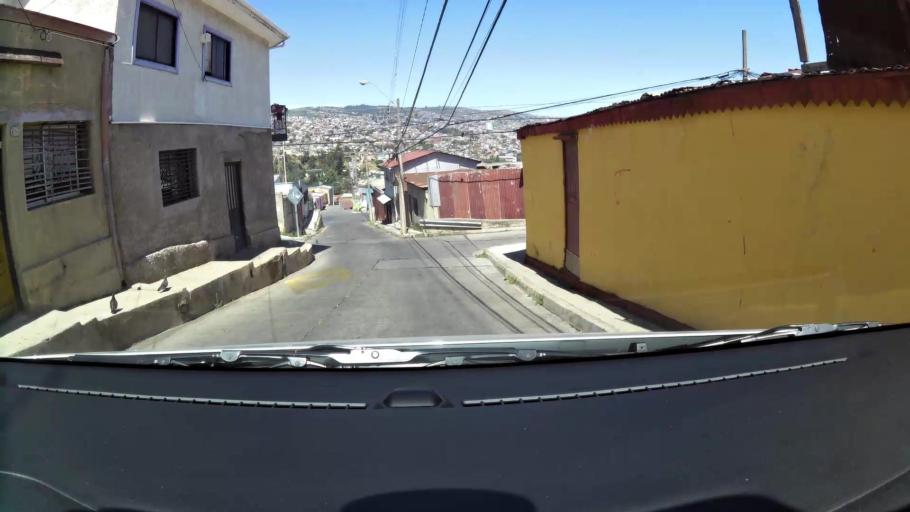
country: CL
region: Valparaiso
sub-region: Provincia de Valparaiso
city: Valparaiso
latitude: -33.0512
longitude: -71.5965
